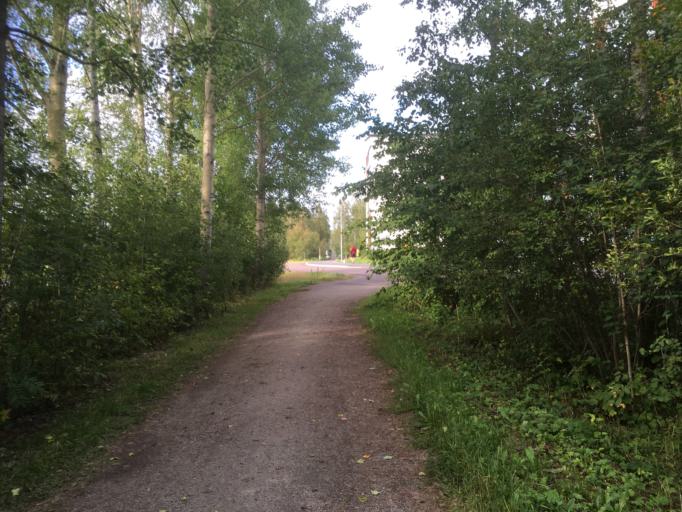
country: FI
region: Central Finland
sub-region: Jyvaeskylae
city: Jyvaeskylae
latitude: 62.2273
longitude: 25.7803
